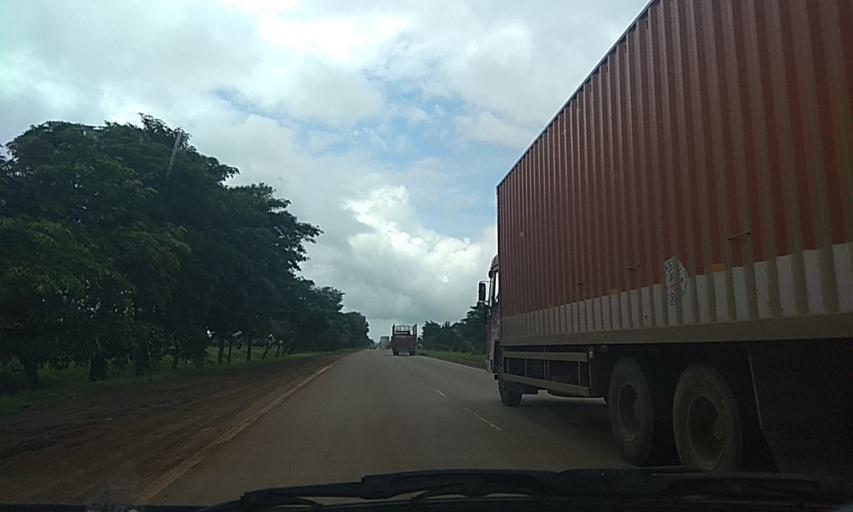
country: IN
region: Karnataka
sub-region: Belgaum
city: Sankeshwar
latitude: 16.2981
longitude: 74.4360
